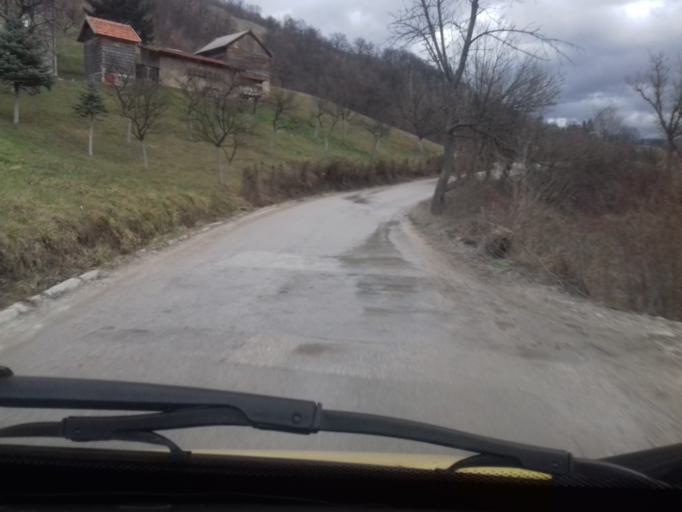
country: BA
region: Federation of Bosnia and Herzegovina
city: Zenica
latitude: 44.2182
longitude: 17.9543
